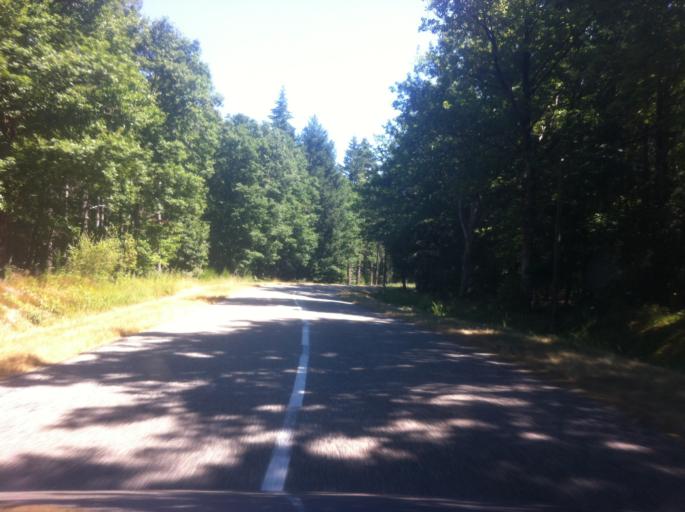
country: FR
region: Auvergne
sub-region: Departement de l'Allier
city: Bellenaves
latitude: 46.2423
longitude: 3.0897
